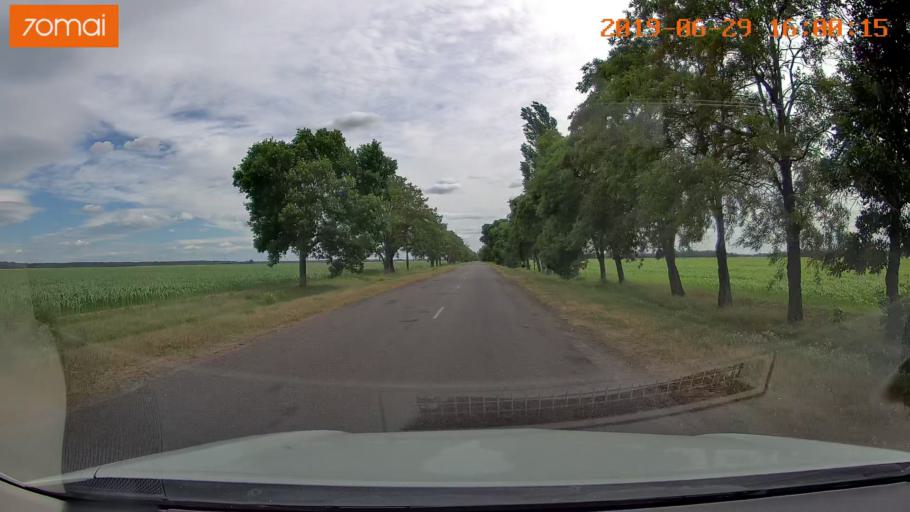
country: BY
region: Brest
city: Luninyets
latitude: 52.2624
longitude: 27.0175
